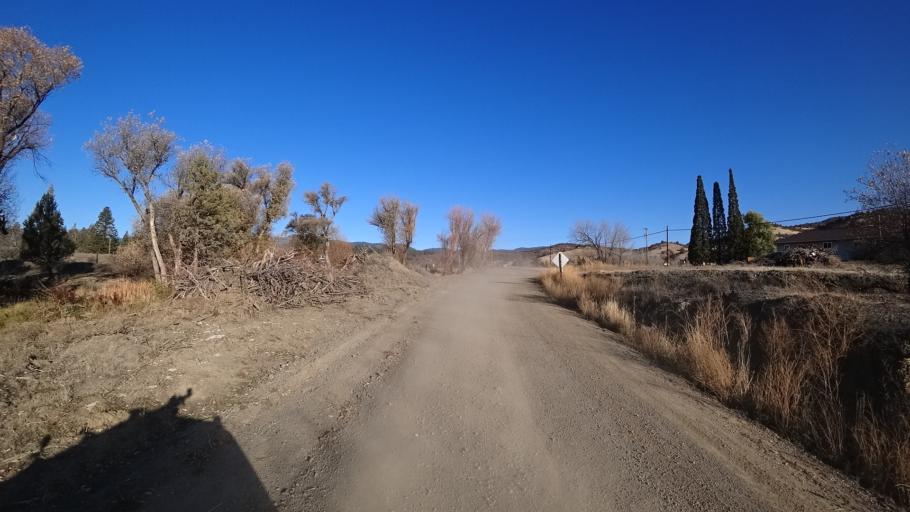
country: US
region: Oregon
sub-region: Jackson County
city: Ashland
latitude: 41.9930
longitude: -122.6239
